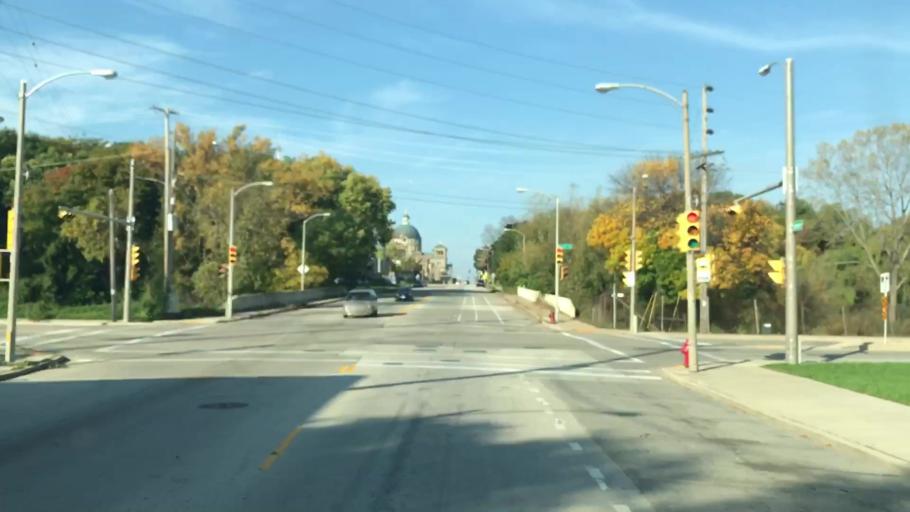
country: US
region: Wisconsin
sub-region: Milwaukee County
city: Milwaukee
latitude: 43.0029
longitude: -87.9109
